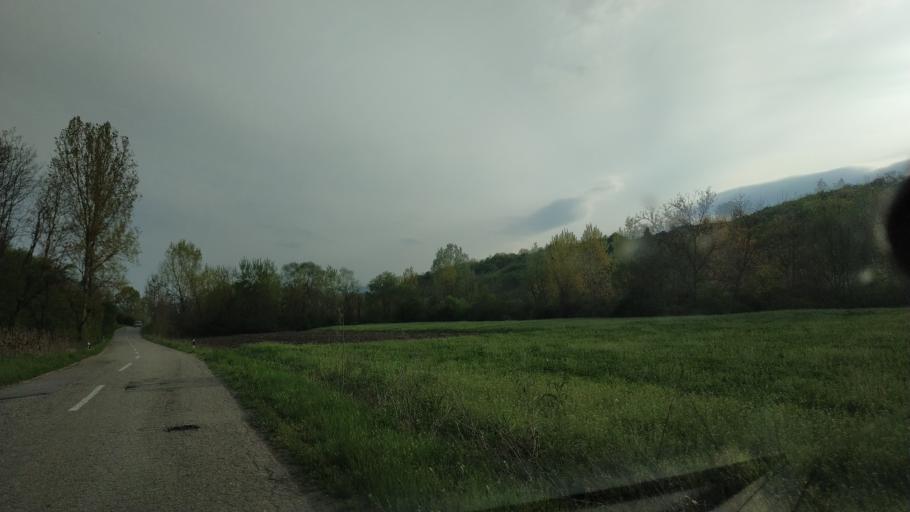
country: RS
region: Central Serbia
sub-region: Nisavski Okrug
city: Aleksinac
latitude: 43.4587
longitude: 21.8013
